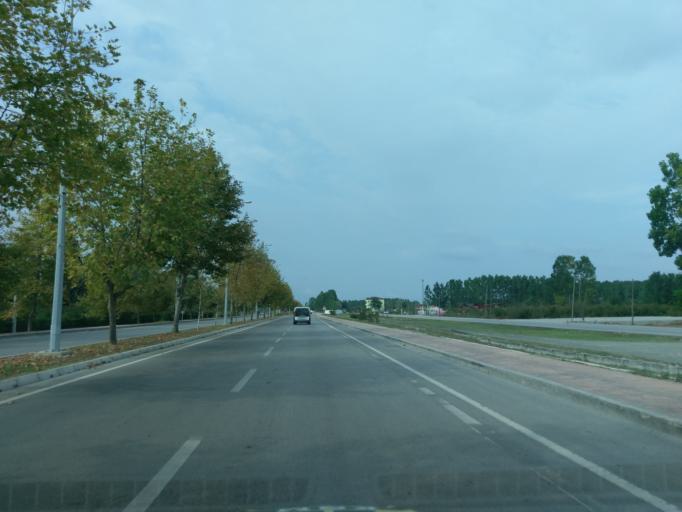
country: TR
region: Samsun
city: Dikbiyik
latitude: 41.2396
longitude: 36.5397
